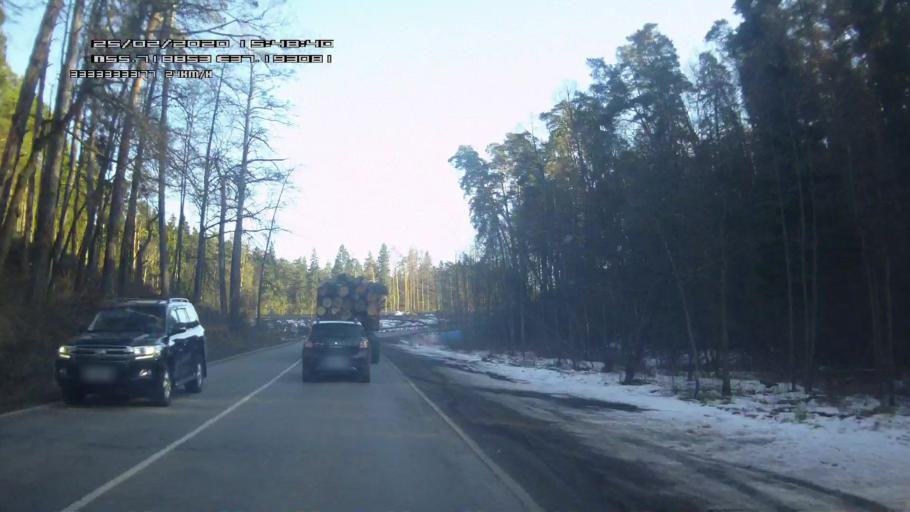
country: RU
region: Moskovskaya
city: Gorki Vtoryye
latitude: 55.7190
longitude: 37.1933
